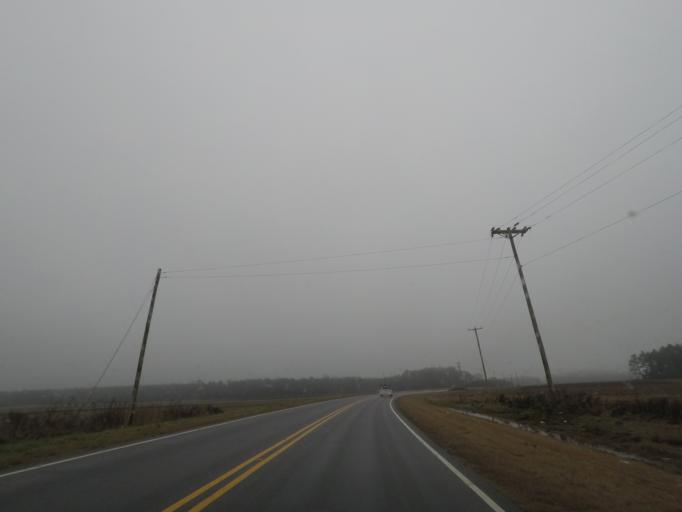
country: US
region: North Carolina
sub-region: Scotland County
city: Laurinburg
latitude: 34.7945
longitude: -79.4275
